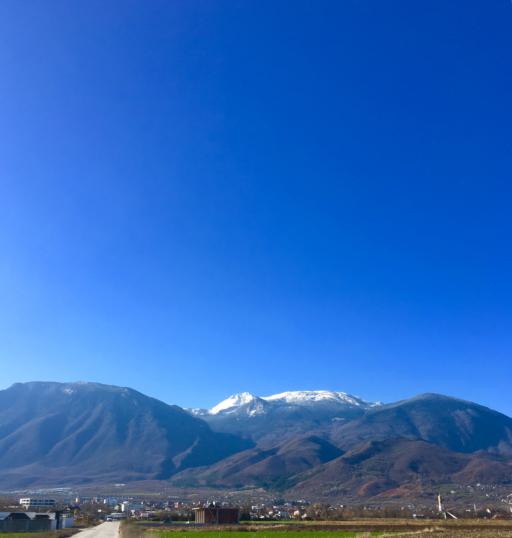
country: XK
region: Pec
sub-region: Komuna e Pejes
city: Peje
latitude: 42.6478
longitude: 20.3200
